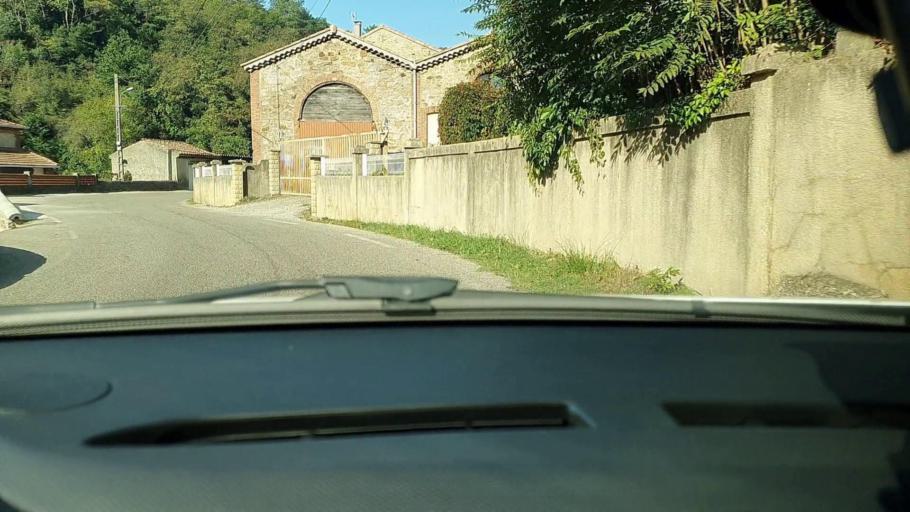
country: FR
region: Languedoc-Roussillon
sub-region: Departement du Gard
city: Besseges
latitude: 44.2806
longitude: 4.0988
